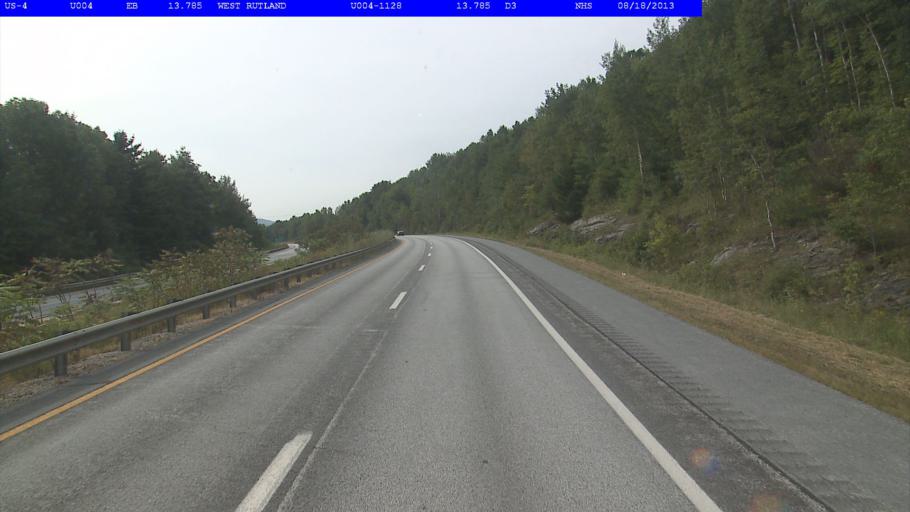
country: US
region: Vermont
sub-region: Rutland County
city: West Rutland
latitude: 43.5961
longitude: -73.0568
